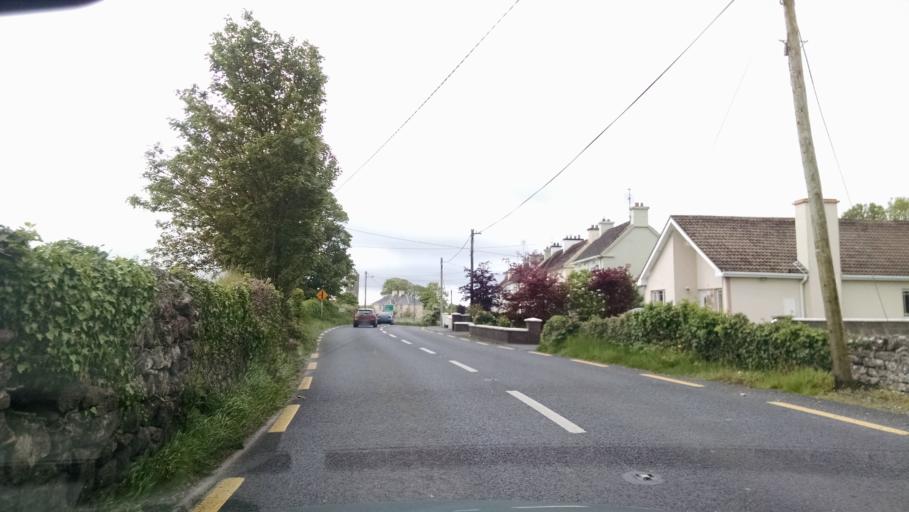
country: IE
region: Connaught
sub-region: County Galway
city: Moycullen
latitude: 53.4762
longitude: -9.0935
